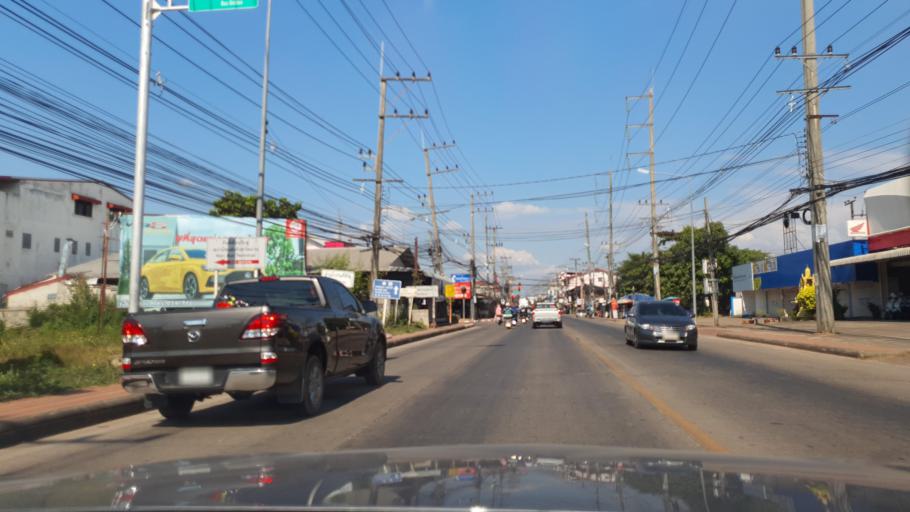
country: TH
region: Nan
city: Nan
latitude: 18.7722
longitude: 100.7652
